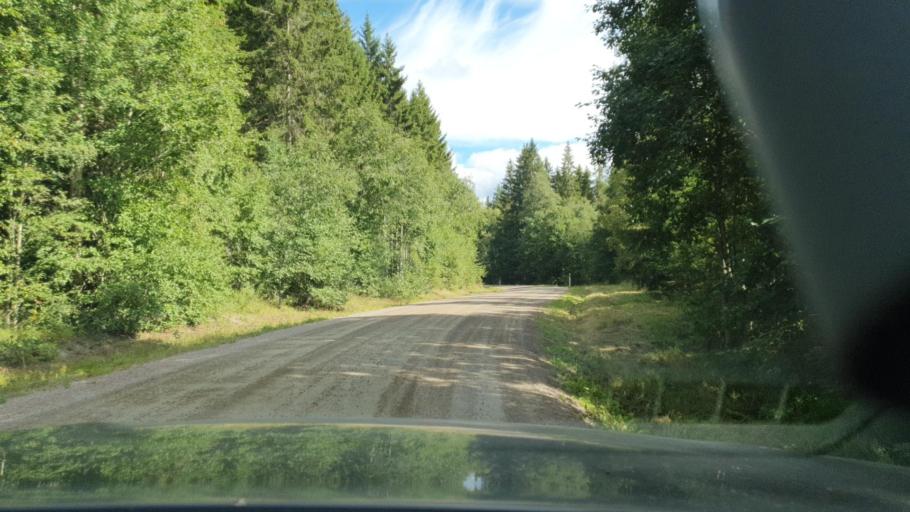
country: SE
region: Vaermland
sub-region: Filipstads Kommun
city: Filipstad
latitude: 59.5697
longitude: 14.1201
